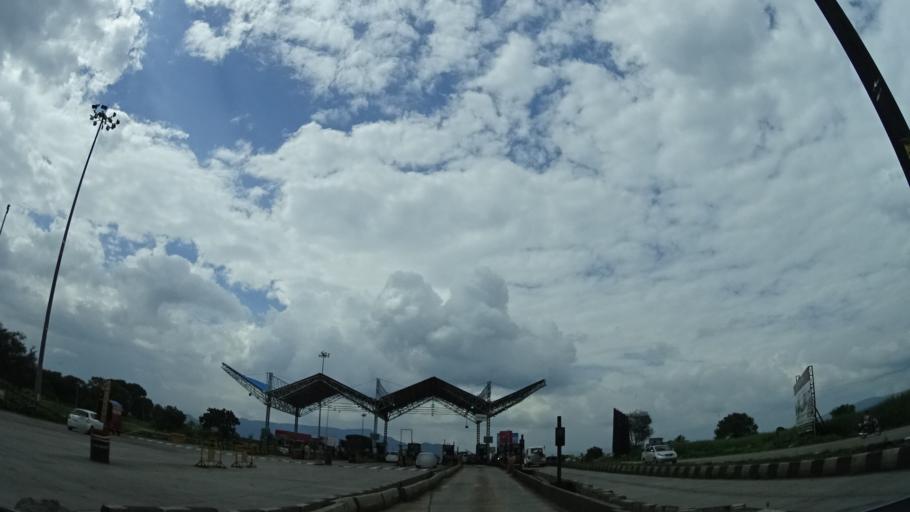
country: IN
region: Maharashtra
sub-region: Satara Division
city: Satara
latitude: 17.8115
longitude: 73.9707
